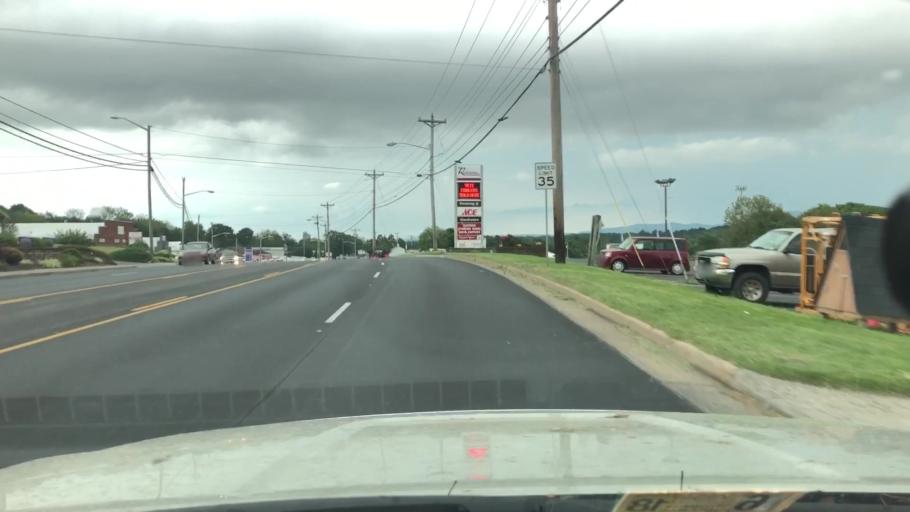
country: US
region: Virginia
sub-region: City of Harrisonburg
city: Harrisonburg
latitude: 38.4381
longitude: -78.8890
